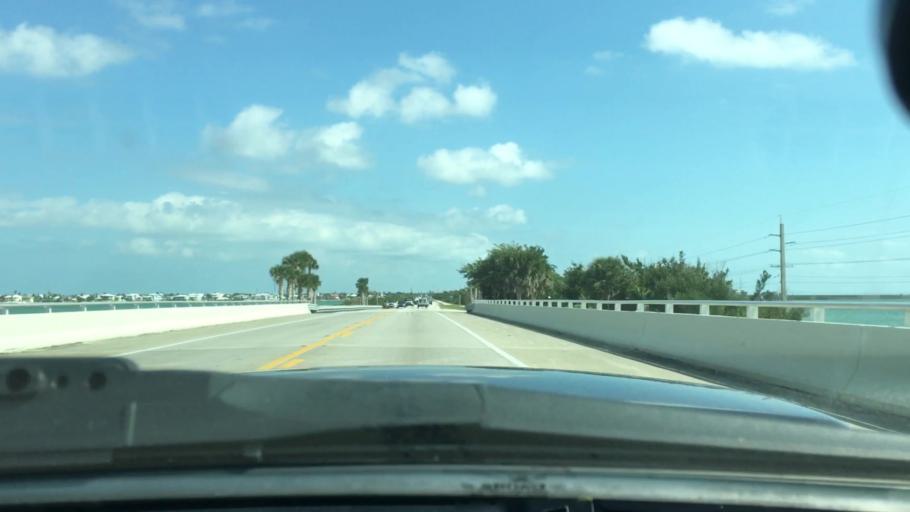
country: US
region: Florida
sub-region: Monroe County
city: Big Pine Key
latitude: 24.6673
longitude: -81.3842
